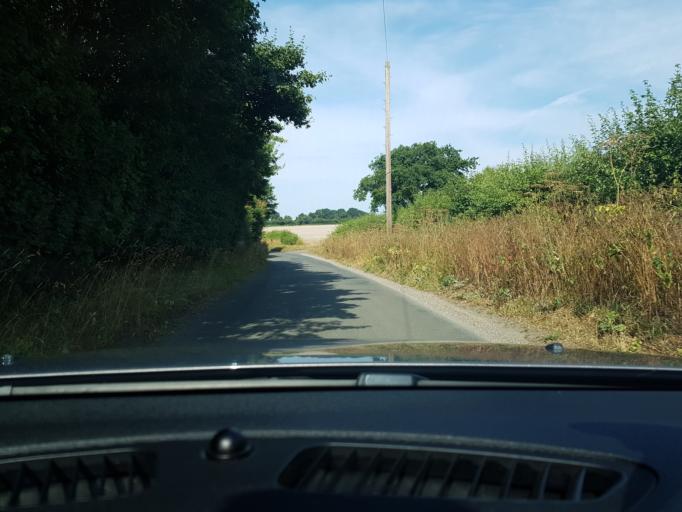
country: GB
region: England
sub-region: West Berkshire
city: Hungerford
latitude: 51.4426
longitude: -1.4936
